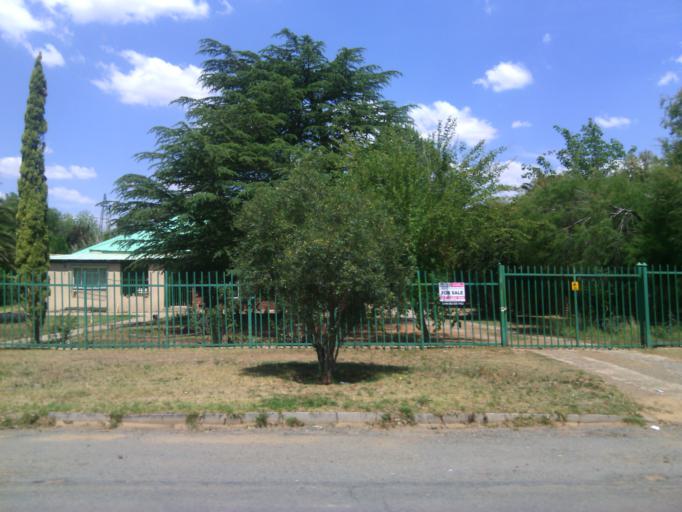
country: ZA
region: Orange Free State
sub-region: Xhariep District Municipality
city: Dewetsdorp
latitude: -29.5814
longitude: 26.6682
